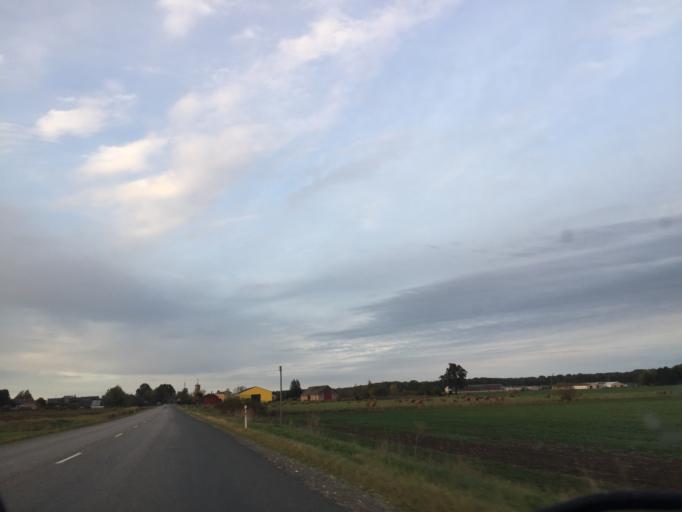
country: LV
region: Dobeles Rajons
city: Dobele
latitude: 56.7305
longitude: 23.3905
